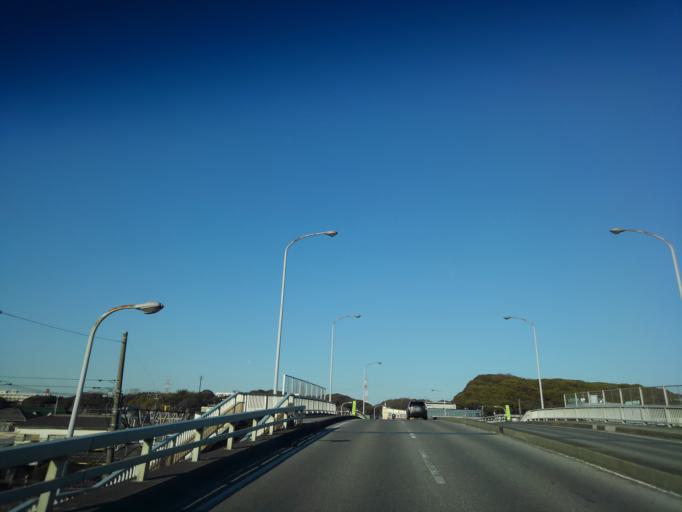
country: JP
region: Chiba
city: Kimitsu
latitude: 35.3348
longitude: 139.8898
